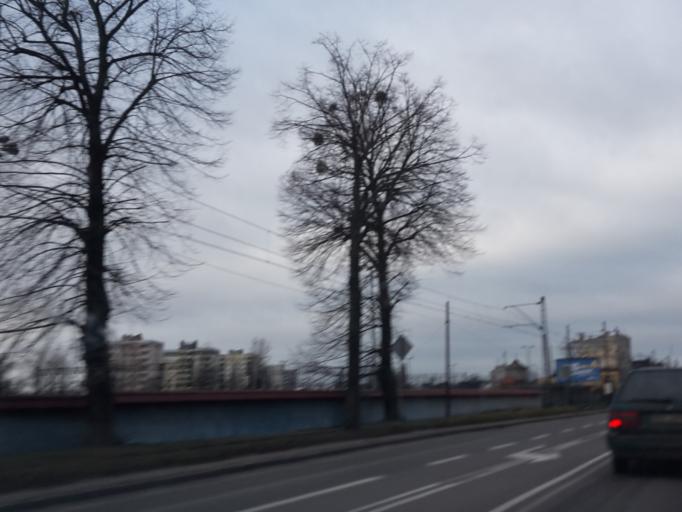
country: PL
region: Warmian-Masurian Voivodeship
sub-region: Powiat elblaski
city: Elblag
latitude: 54.1498
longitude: 19.4254
